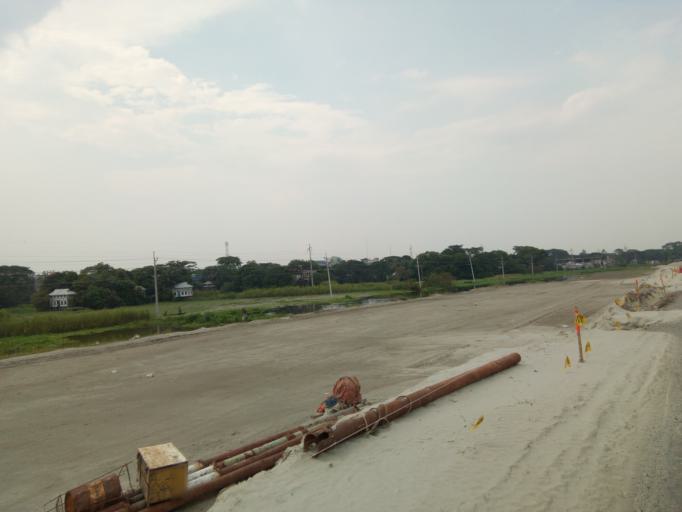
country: BD
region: Dhaka
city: Dohar
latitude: 23.5319
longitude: 90.2906
